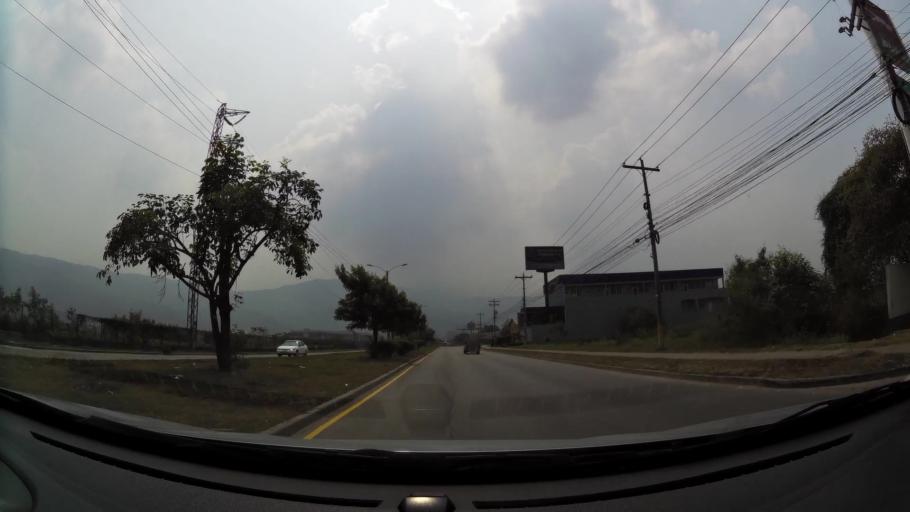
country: HN
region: Cortes
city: San Pedro Sula
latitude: 15.4735
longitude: -88.0140
